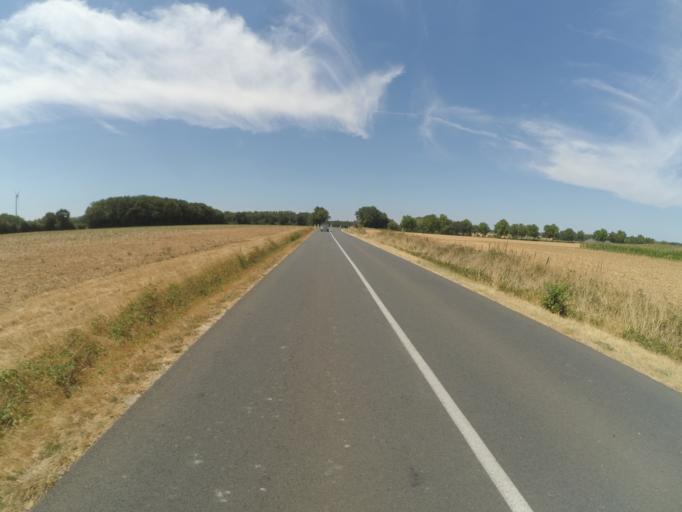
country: FR
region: Poitou-Charentes
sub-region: Departement de la Vienne
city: Saint-Maurice-la-Clouere
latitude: 46.3318
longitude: 0.4687
